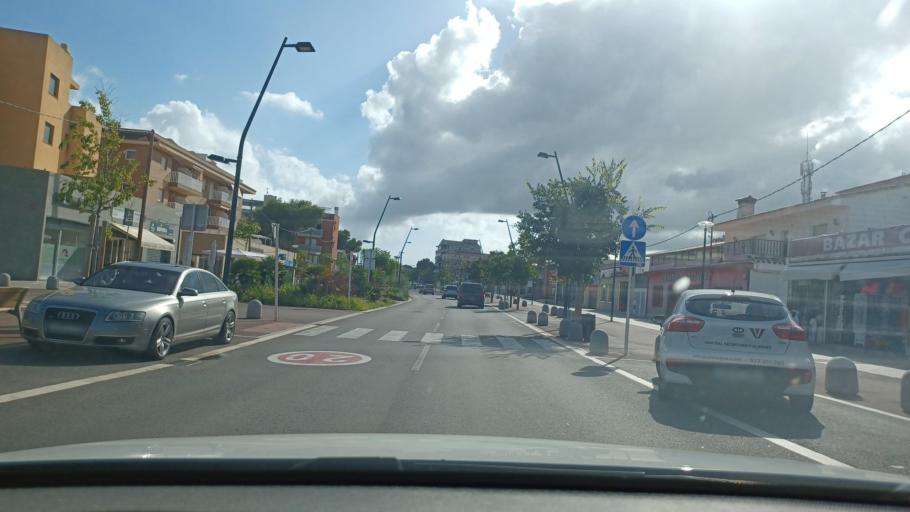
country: ES
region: Catalonia
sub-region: Provincia de Tarragona
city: Colldejou
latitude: 41.0092
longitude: 0.9389
